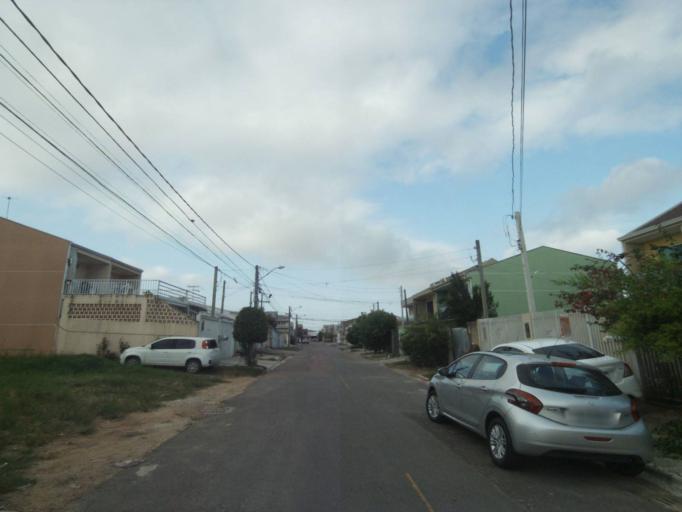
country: BR
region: Parana
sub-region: Sao Jose Dos Pinhais
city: Sao Jose dos Pinhais
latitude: -25.5489
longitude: -49.2557
